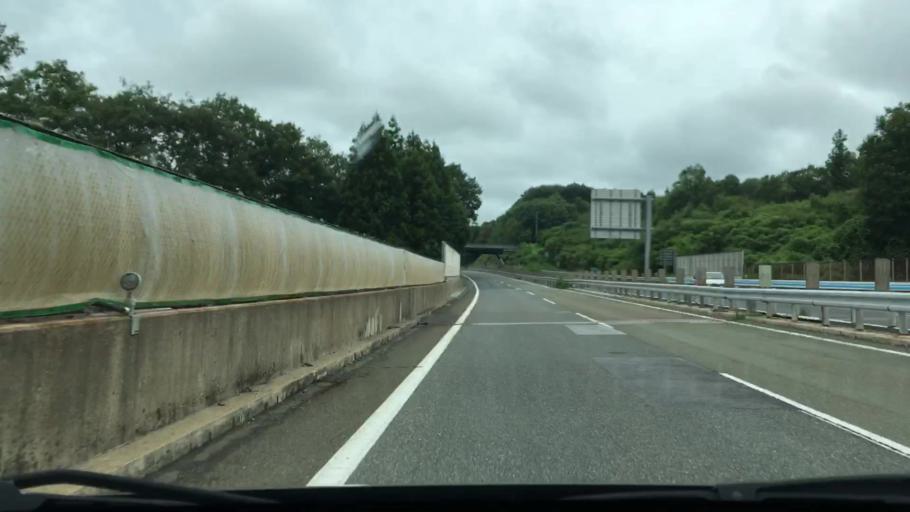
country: JP
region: Hiroshima
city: Miyoshi
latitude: 34.7954
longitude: 132.8880
